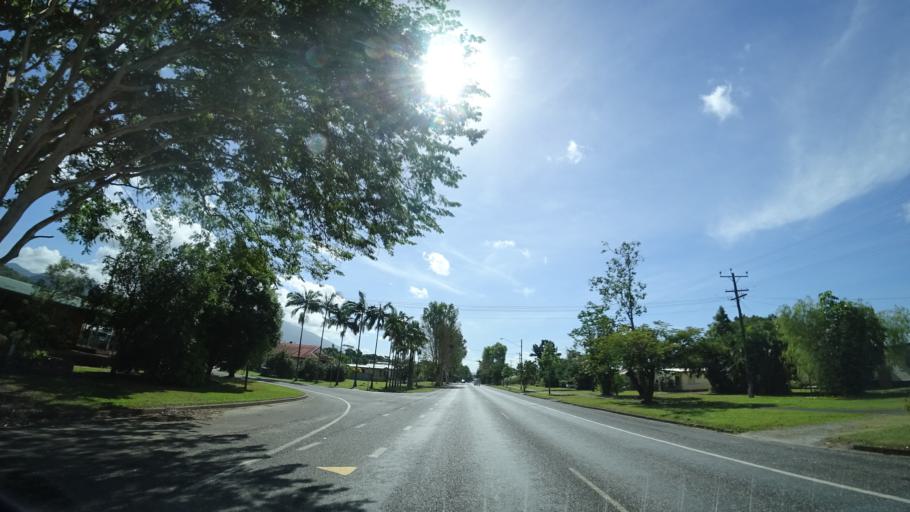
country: AU
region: Queensland
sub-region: Cairns
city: Port Douglas
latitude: -16.4740
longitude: 145.3745
